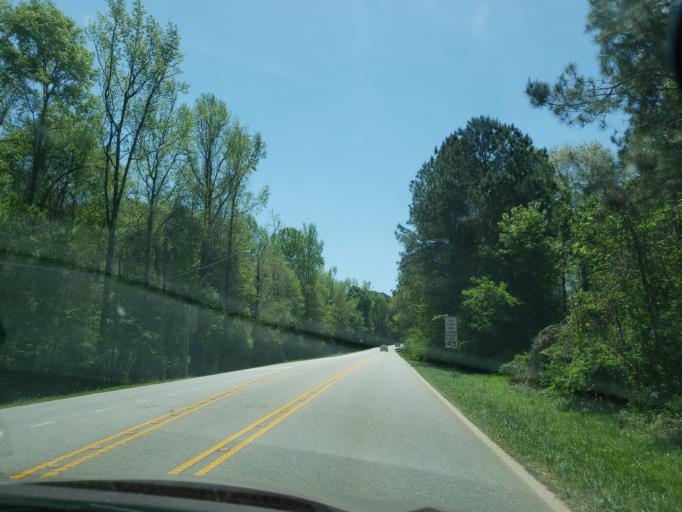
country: US
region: Alabama
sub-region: Lee County
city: Auburn
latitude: 32.6396
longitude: -85.5027
